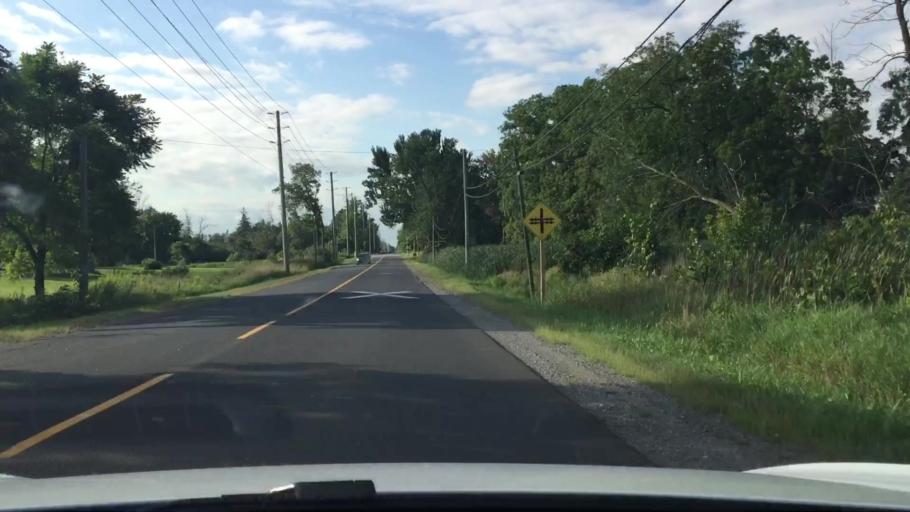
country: CA
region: Ontario
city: Markham
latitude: 43.8743
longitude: -79.2081
